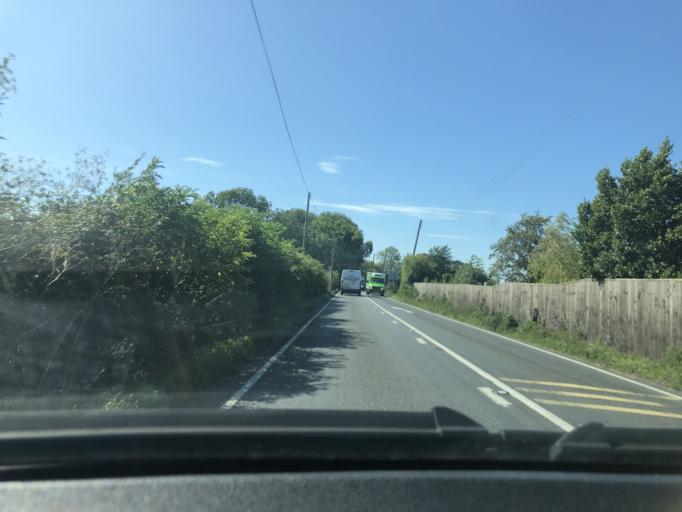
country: GB
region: England
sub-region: Somerset
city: Woolavington
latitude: 51.1468
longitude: -2.8995
